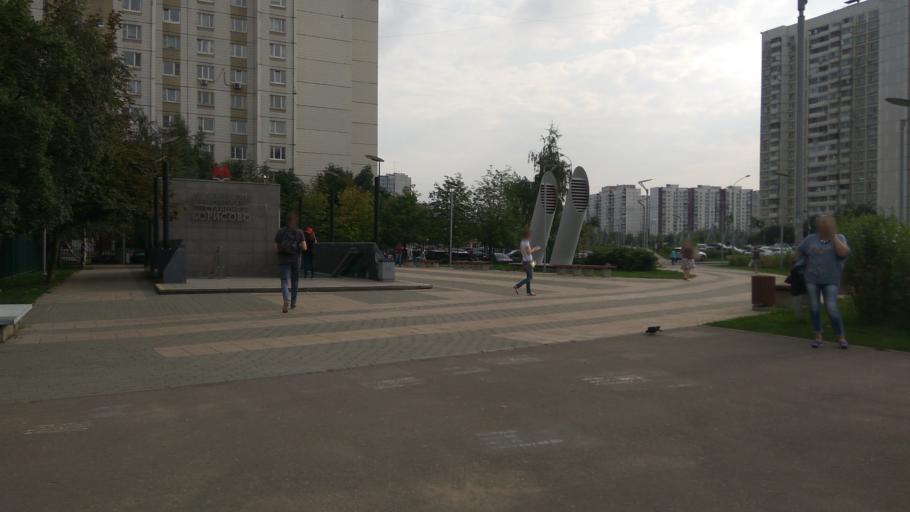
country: RU
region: Moscow
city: Brateyevo
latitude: 55.6343
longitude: 37.7446
